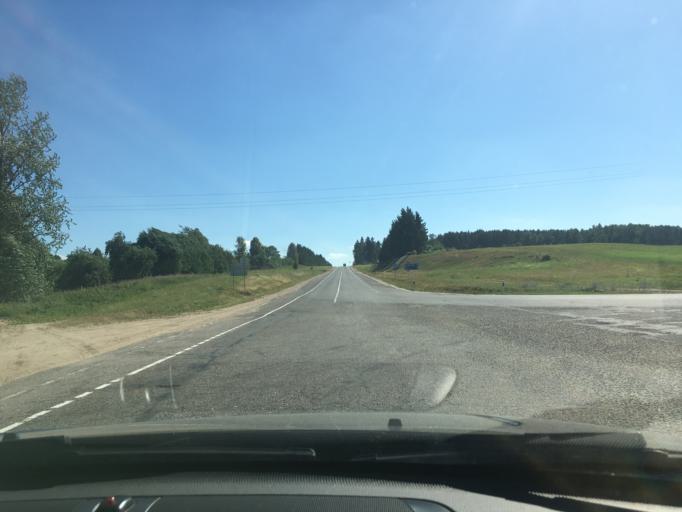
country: BY
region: Grodnenskaya
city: Hal'shany
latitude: 54.2537
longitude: 26.0071
